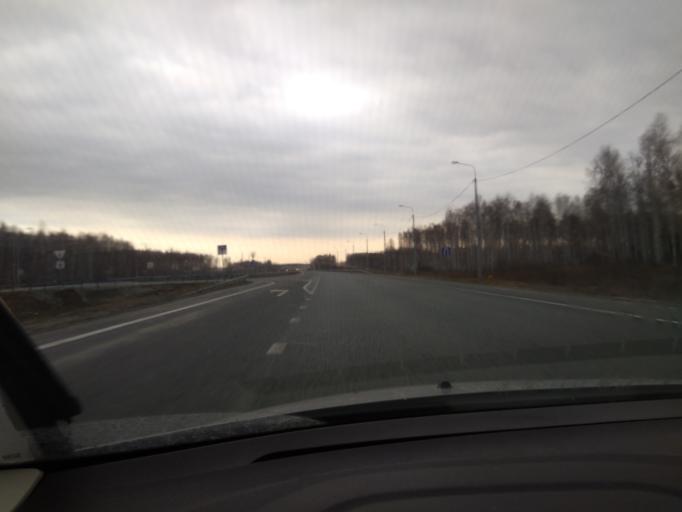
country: RU
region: Chelyabinsk
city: Kunashak
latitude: 55.7664
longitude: 61.2191
